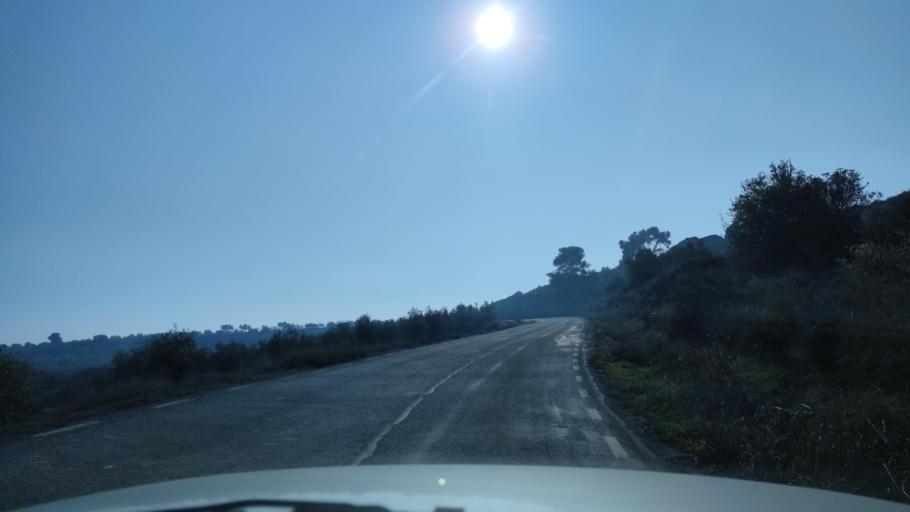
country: ES
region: Catalonia
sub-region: Provincia de Lleida
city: Torrebesses
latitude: 41.4534
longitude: 0.5578
